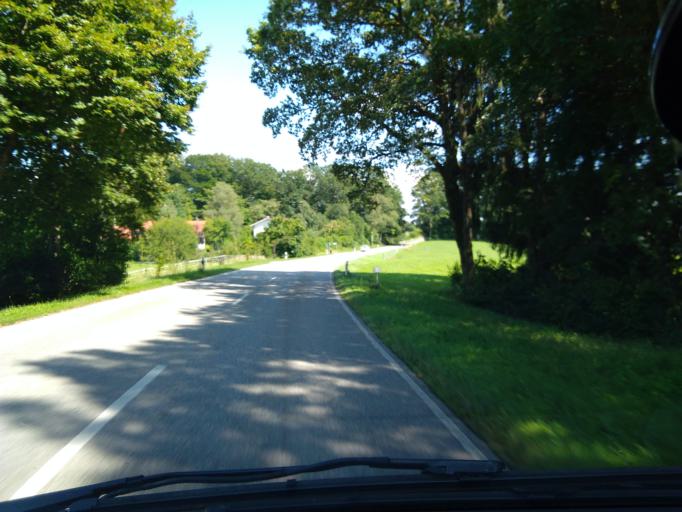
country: DE
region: Bavaria
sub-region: Upper Bavaria
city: Emmering
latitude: 47.9912
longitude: 12.0368
